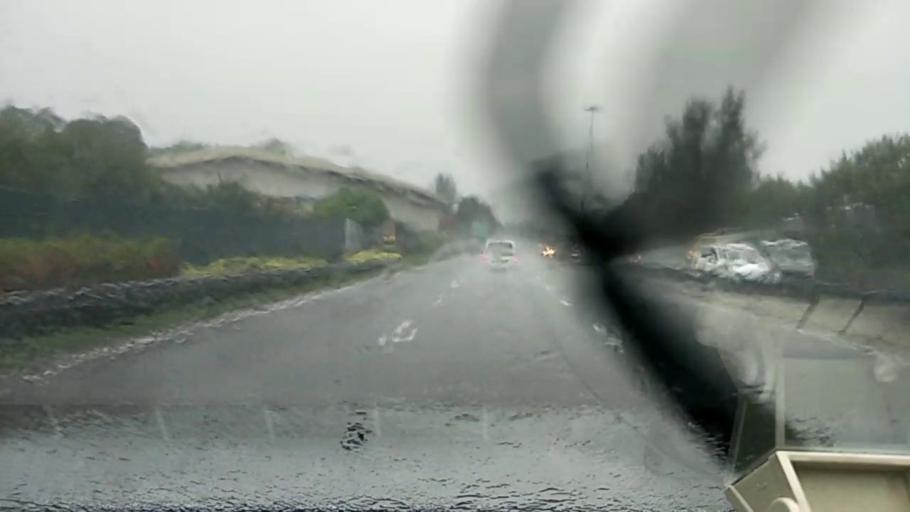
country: MY
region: Selangor
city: Kampong Baharu Balakong
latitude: 3.0026
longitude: 101.7733
